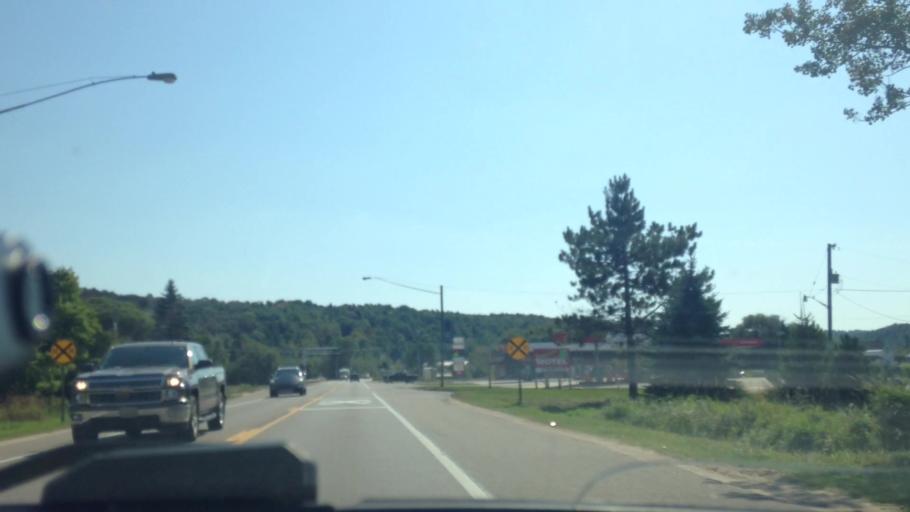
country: US
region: Michigan
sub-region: Alger County
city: Munising
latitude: 46.4047
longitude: -86.6496
